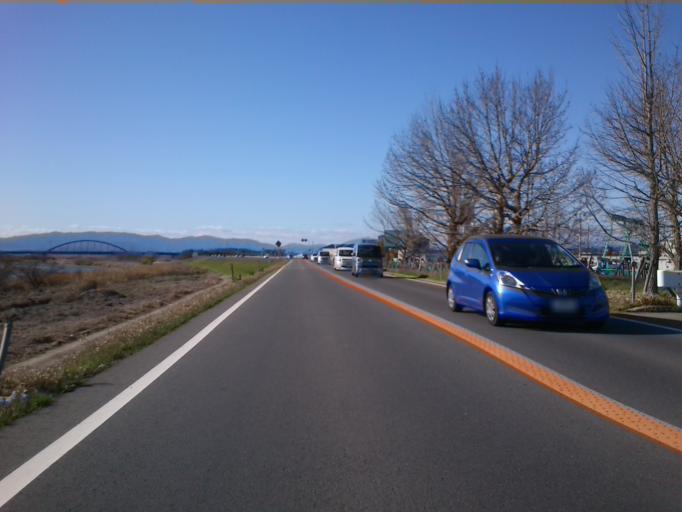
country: JP
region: Kyoto
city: Tanabe
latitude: 34.8149
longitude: 135.8018
